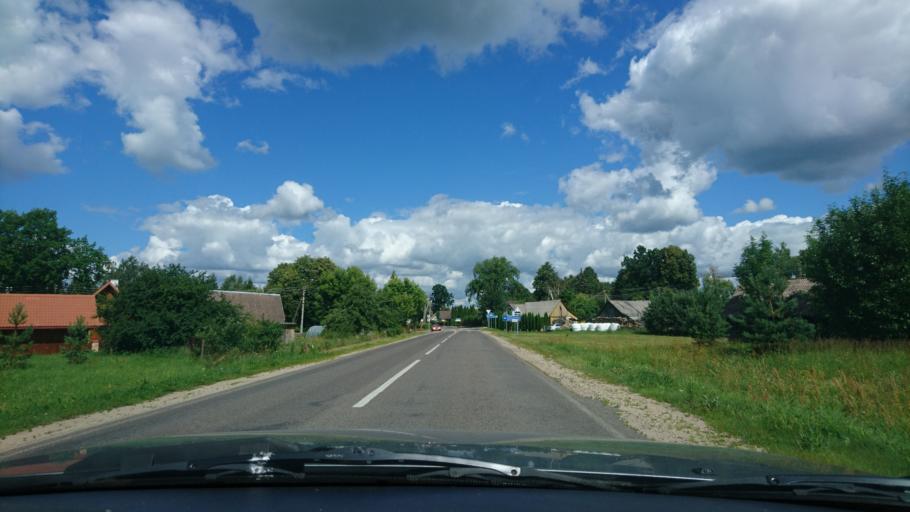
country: LT
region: Panevezys
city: Rokiskis
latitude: 55.7510
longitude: 25.8466
